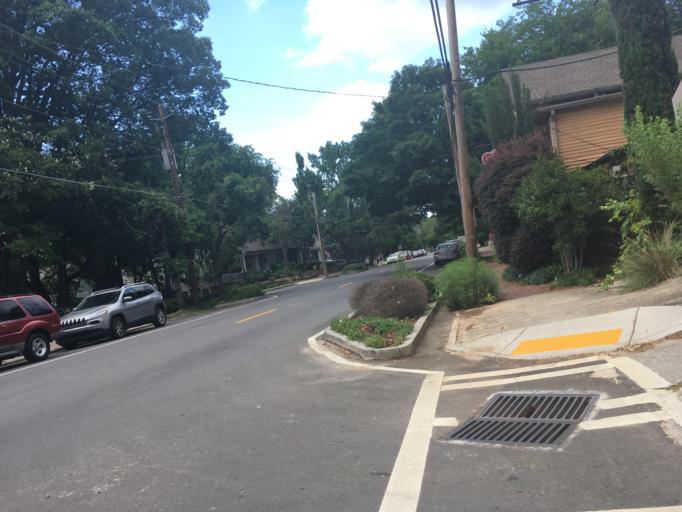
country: US
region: Georgia
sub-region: Fulton County
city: Atlanta
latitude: 33.7579
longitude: -84.3625
